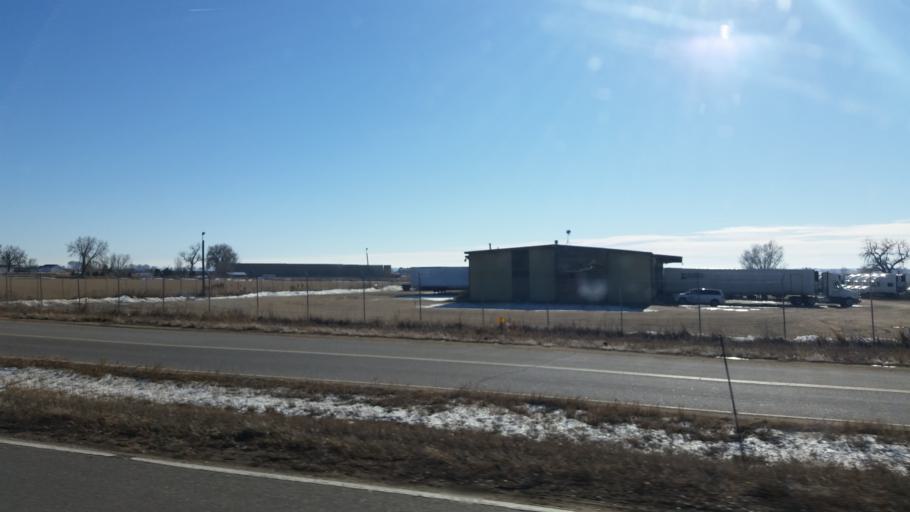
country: US
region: Colorado
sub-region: Weld County
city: Johnstown
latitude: 40.4071
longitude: -104.9493
